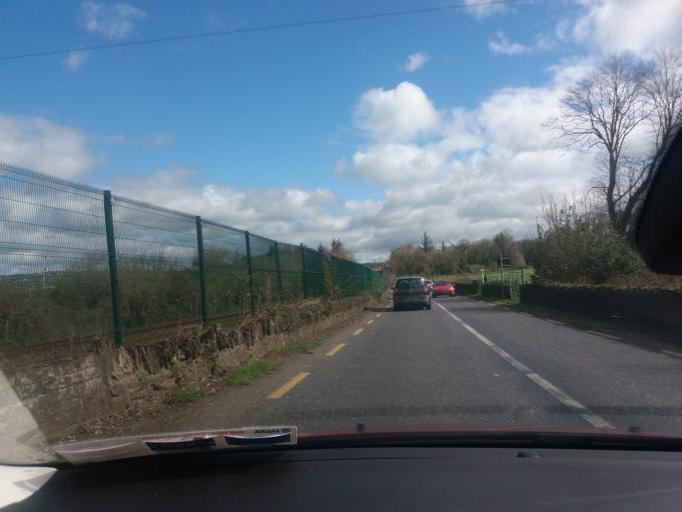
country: IE
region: Munster
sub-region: County Cork
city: Passage West
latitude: 51.8784
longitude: -8.3225
